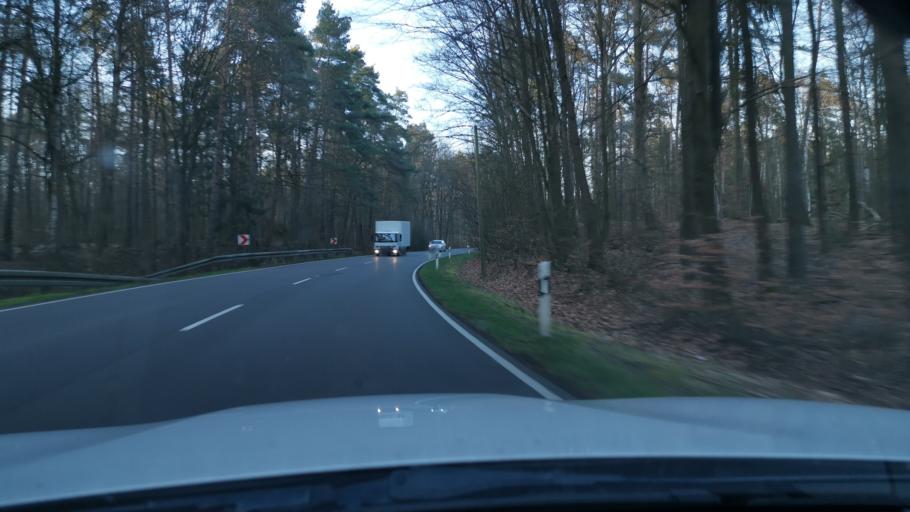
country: DE
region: Saxony
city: Bad Duben
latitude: 51.6717
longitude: 12.6012
